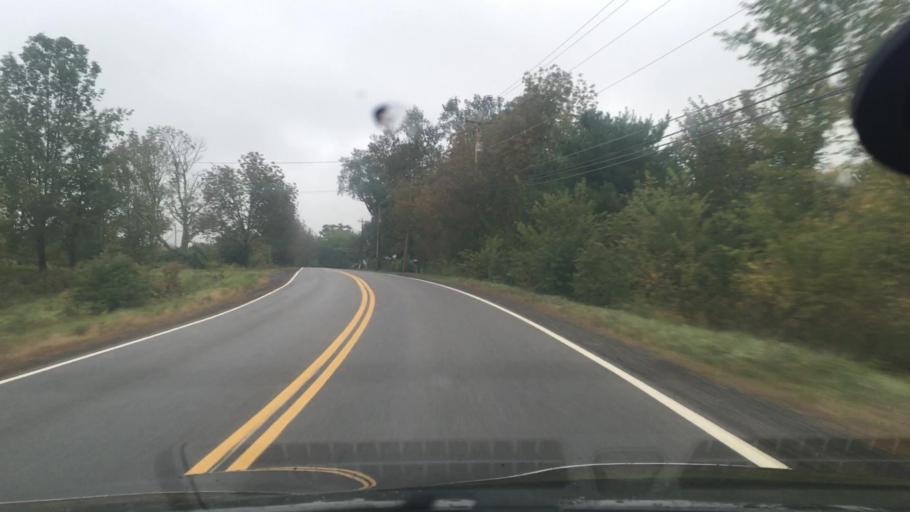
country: CA
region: Nova Scotia
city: Windsor
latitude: 44.9497
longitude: -64.1746
